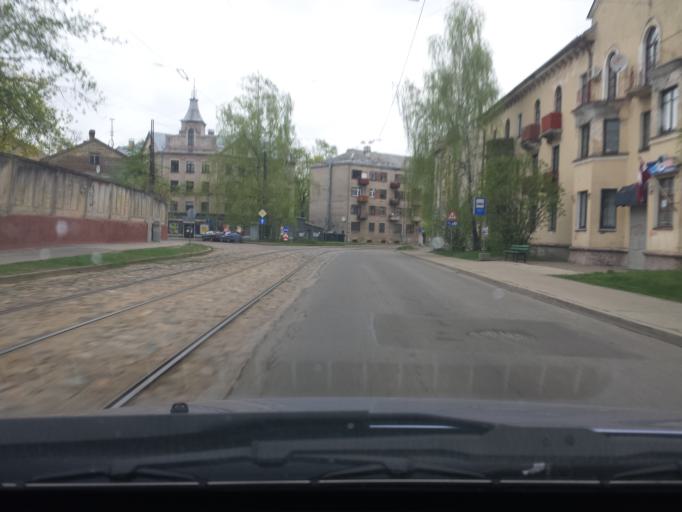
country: LV
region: Riga
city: Riga
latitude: 56.9590
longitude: 24.0605
